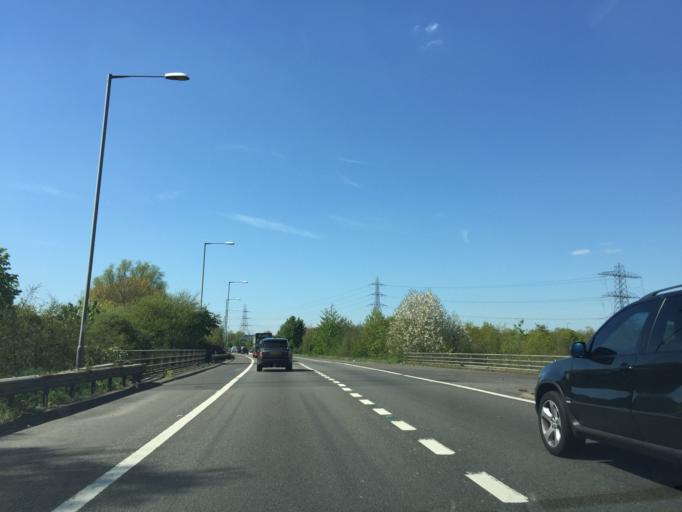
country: GB
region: England
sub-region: Greater London
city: Woodford Green
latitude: 51.5975
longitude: 0.0448
